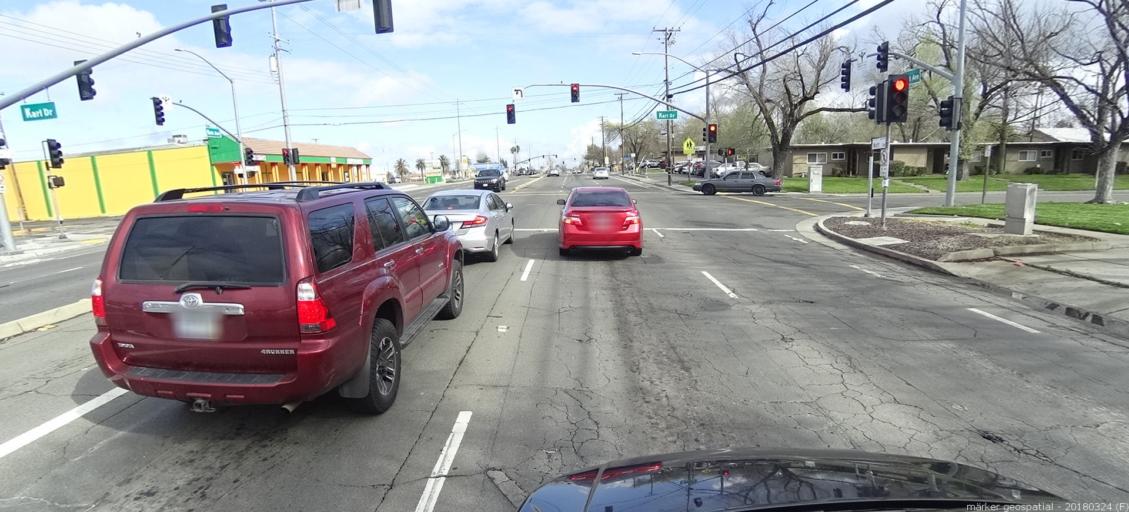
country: US
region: California
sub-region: Sacramento County
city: North Highlands
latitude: 38.6735
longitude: -121.3829
